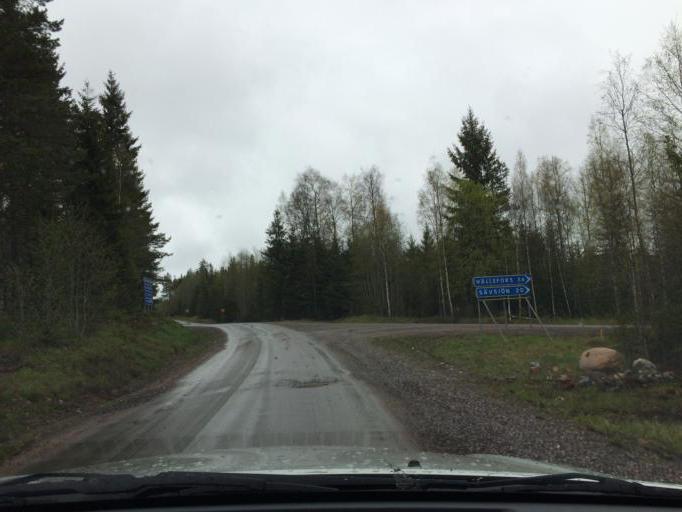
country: SE
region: Dalarna
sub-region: Ludvika Kommun
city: Abborrberget
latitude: 60.0389
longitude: 14.6805
